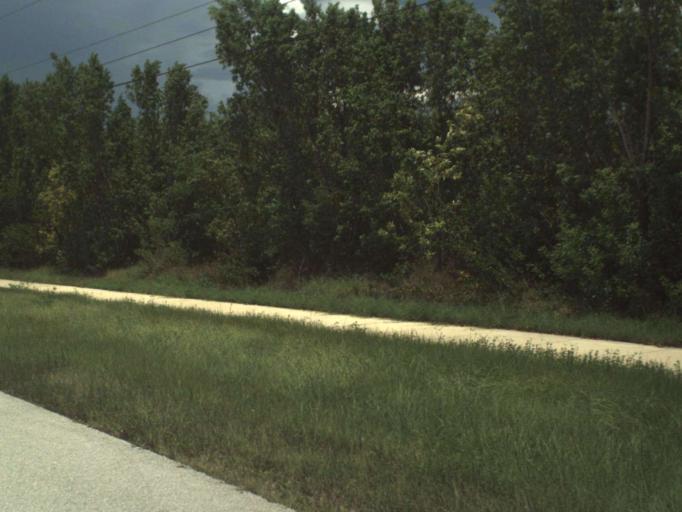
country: US
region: Florida
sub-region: Saint Lucie County
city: Indian River Estates
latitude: 27.4112
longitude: -80.2729
